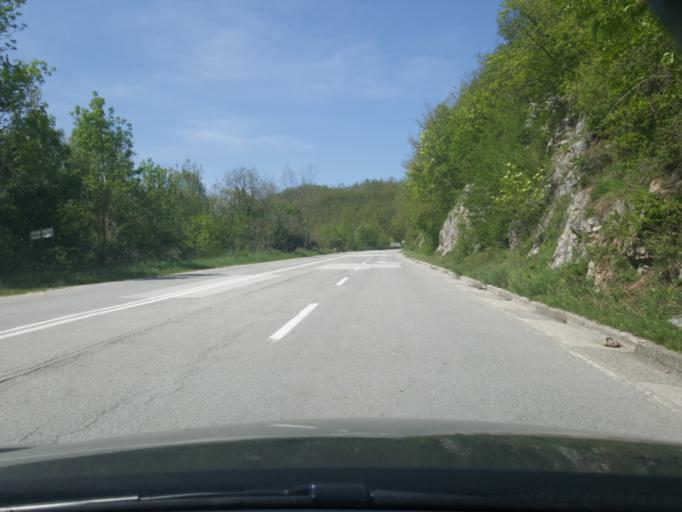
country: RS
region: Central Serbia
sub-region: Zlatiborski Okrug
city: Cajetina
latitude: 43.8054
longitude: 19.6465
